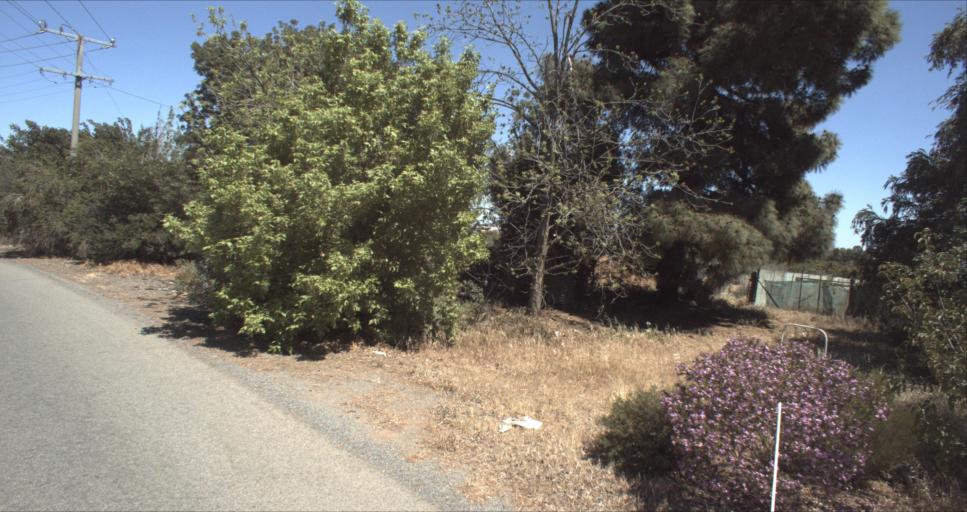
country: AU
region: New South Wales
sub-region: Leeton
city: Leeton
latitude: -34.5425
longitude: 146.3943
